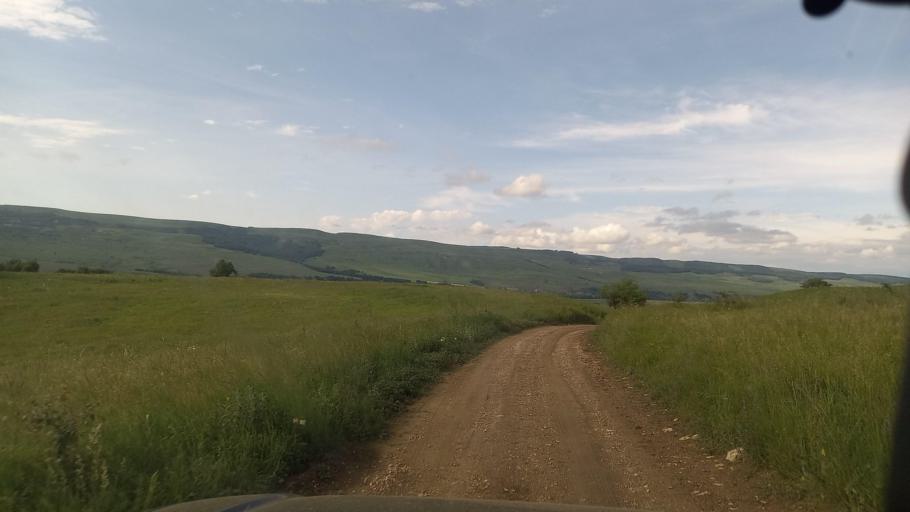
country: RU
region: Krasnodarskiy
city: Peredovaya
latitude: 44.0794
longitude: 41.3642
